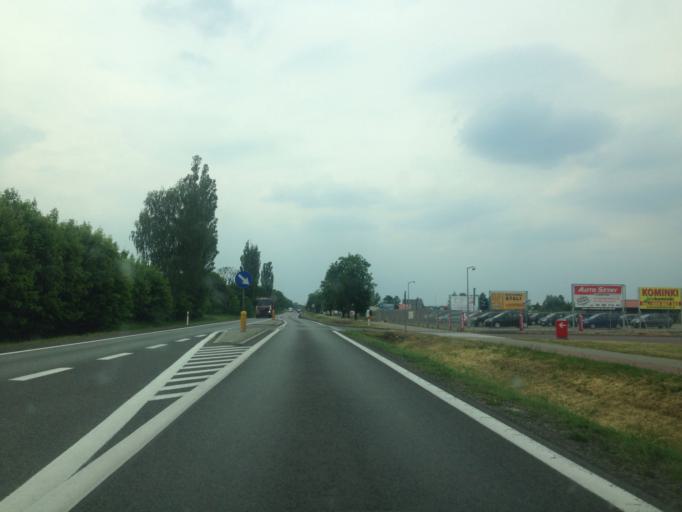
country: PL
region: Kujawsko-Pomorskie
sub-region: Grudziadz
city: Grudziadz
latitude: 53.4886
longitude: 18.7224
